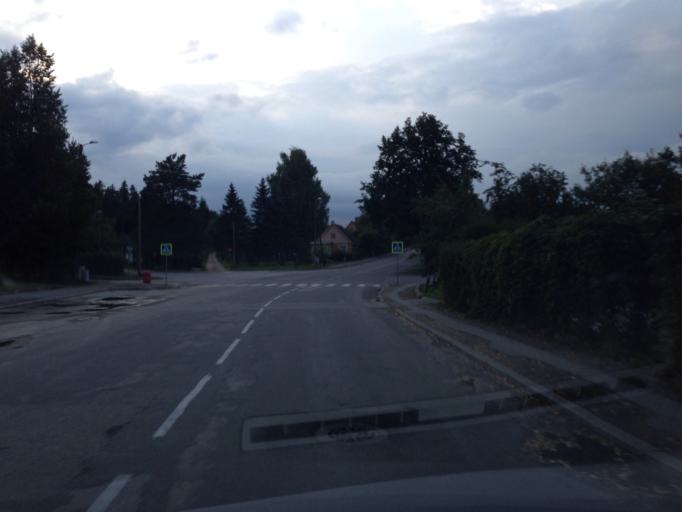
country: EE
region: Tartu
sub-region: Elva linn
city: Elva
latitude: 58.2275
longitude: 26.4166
